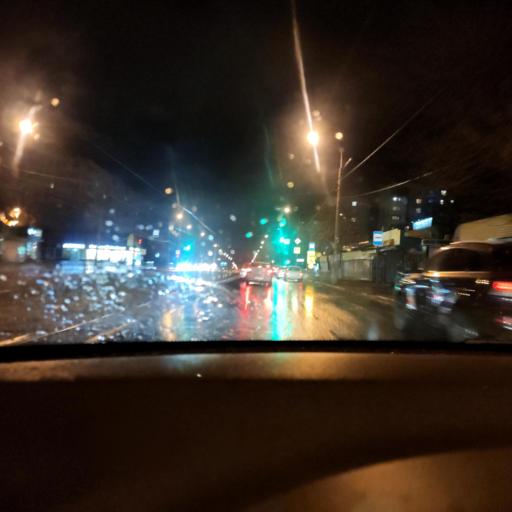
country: RU
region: Samara
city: Samara
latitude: 53.2390
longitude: 50.2150
